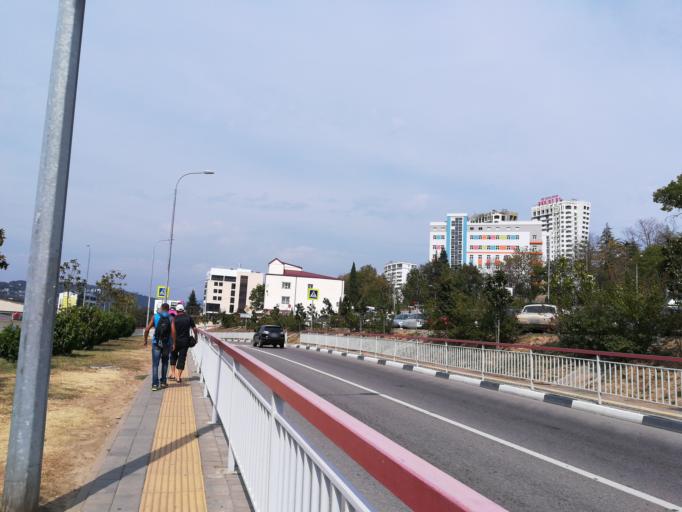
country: RU
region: Krasnodarskiy
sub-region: Sochi City
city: Sochi
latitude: 43.5978
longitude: 39.7320
